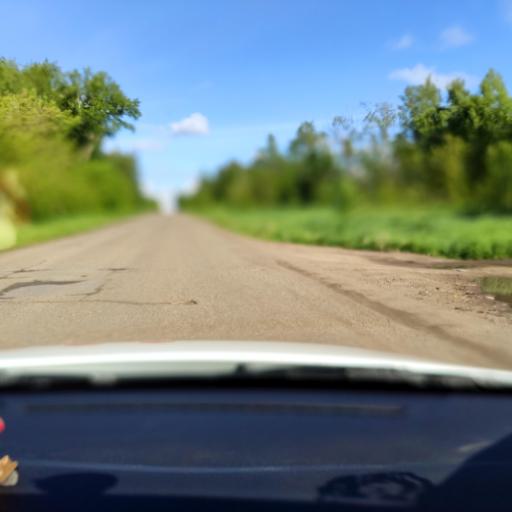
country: RU
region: Tatarstan
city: Stolbishchi
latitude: 55.7208
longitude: 49.2105
